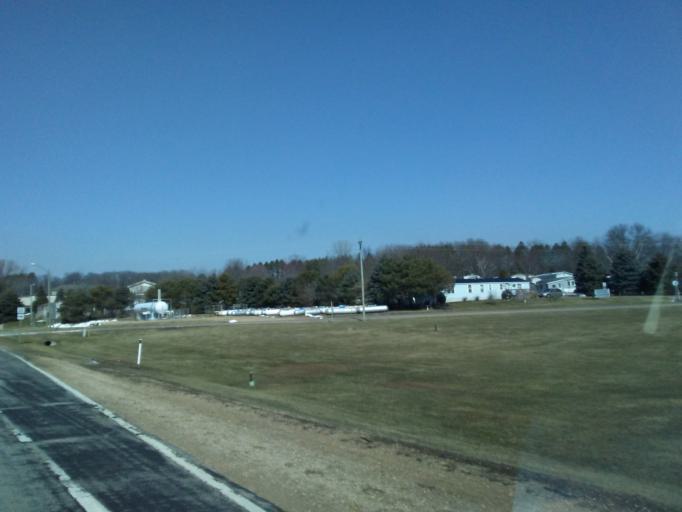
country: US
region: Wisconsin
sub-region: Vernon County
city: Viroqua
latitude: 43.5342
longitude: -90.8744
